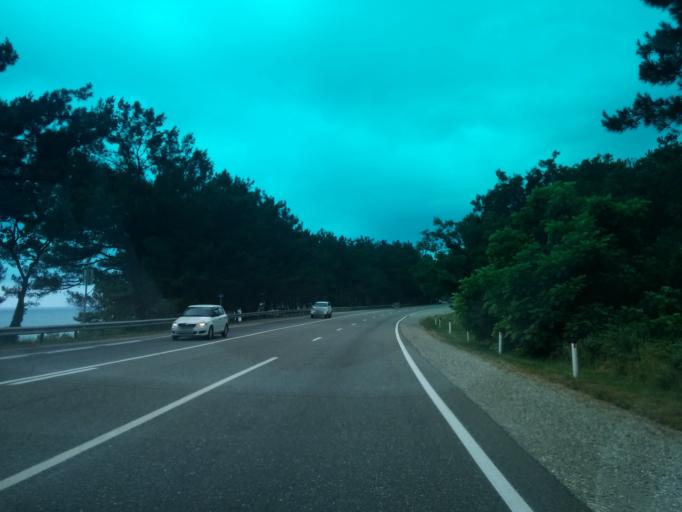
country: RU
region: Krasnodarskiy
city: Ol'ginka
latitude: 44.1848
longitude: 38.9217
